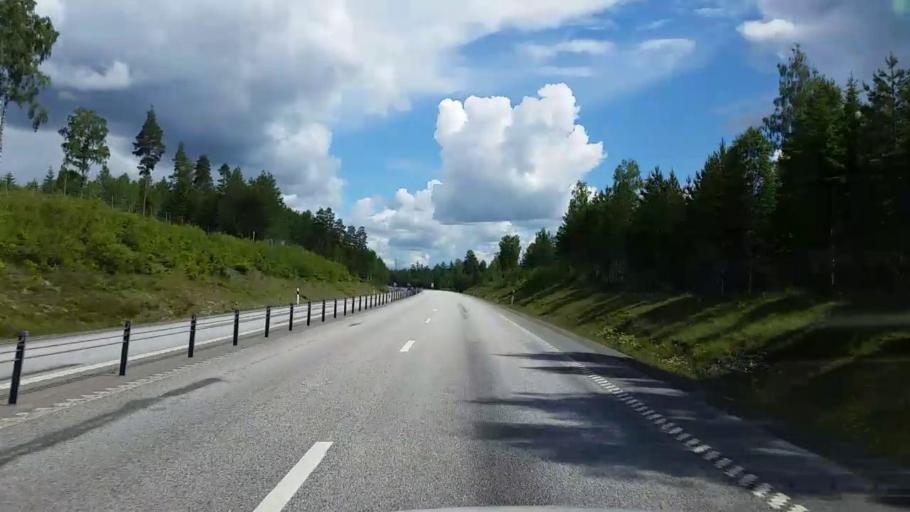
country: SE
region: Vaestmanland
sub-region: Fagersta Kommun
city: Fagersta
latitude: 60.0418
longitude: 15.8250
